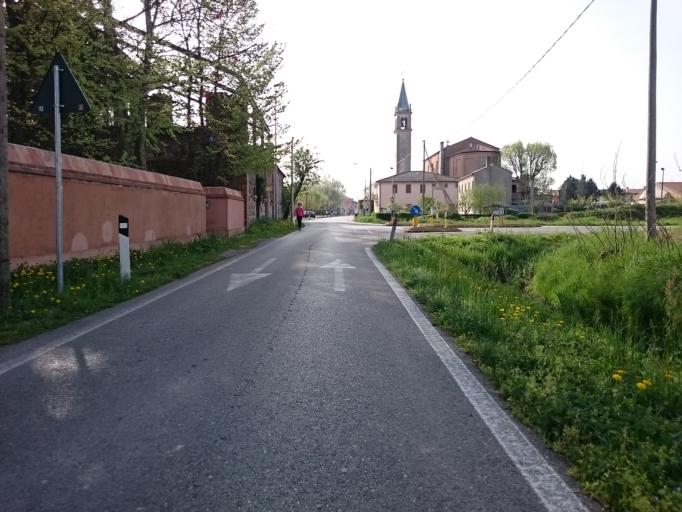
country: IT
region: Veneto
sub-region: Provincia di Padova
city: Masera di Padova
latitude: 45.3322
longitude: 11.8692
